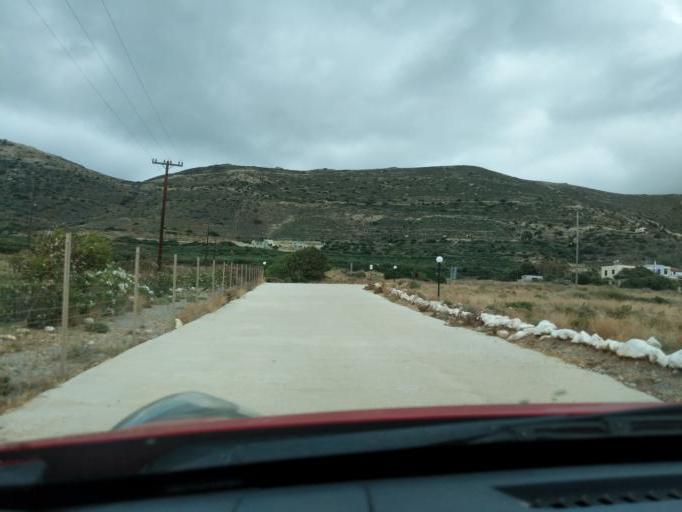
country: GR
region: Crete
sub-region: Nomos Chanias
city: Platanos
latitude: 35.4987
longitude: 23.5813
